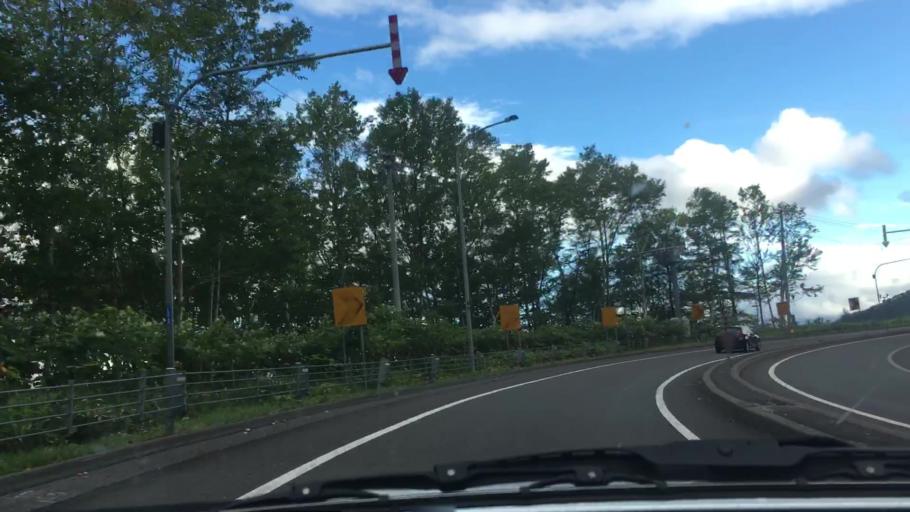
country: JP
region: Hokkaido
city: Shimo-furano
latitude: 43.1482
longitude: 142.7738
